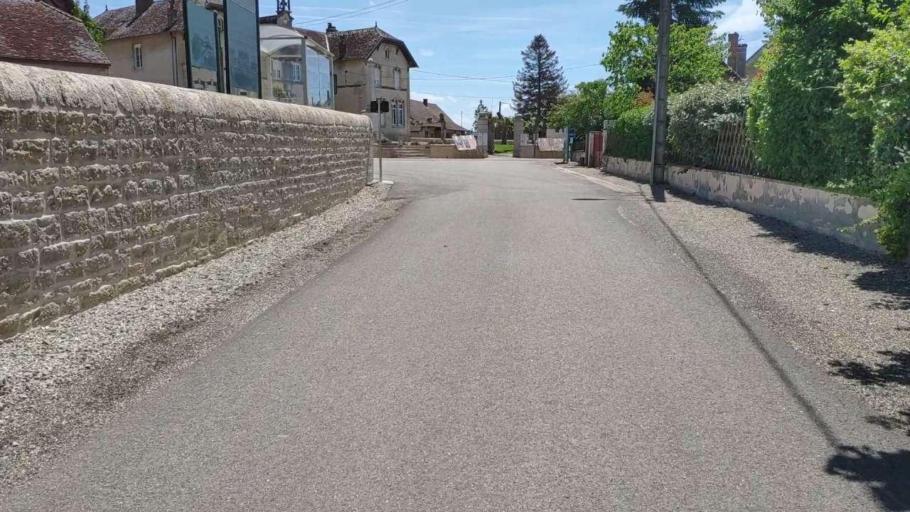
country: FR
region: Franche-Comte
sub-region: Departement du Jura
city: Bletterans
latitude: 46.8027
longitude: 5.3772
